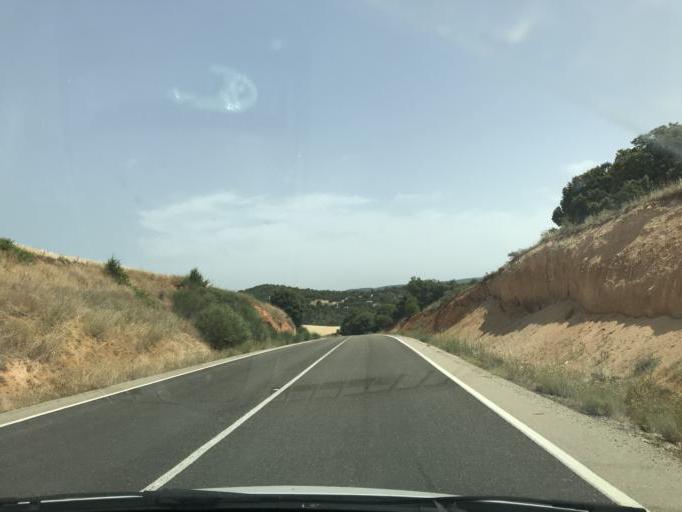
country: ES
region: Castille-La Mancha
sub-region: Provincia de Cuenca
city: Albalate de las Nogueras
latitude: 40.3967
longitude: -2.2550
